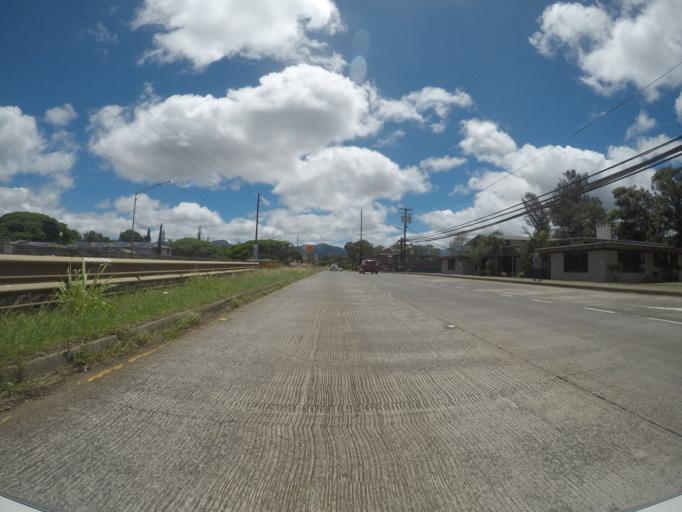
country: US
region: Hawaii
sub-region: Honolulu County
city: Wahiawa
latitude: 21.4901
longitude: -158.0329
